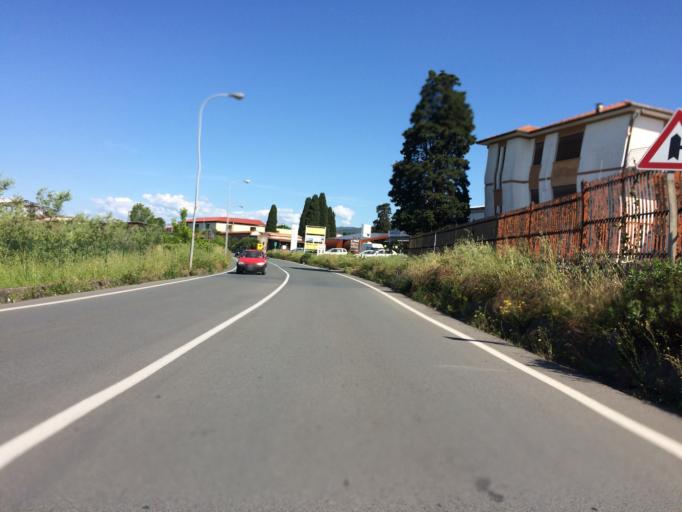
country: IT
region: Liguria
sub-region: Provincia di La Spezia
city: Colombiera-Molicciara
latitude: 44.0880
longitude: 10.0019
